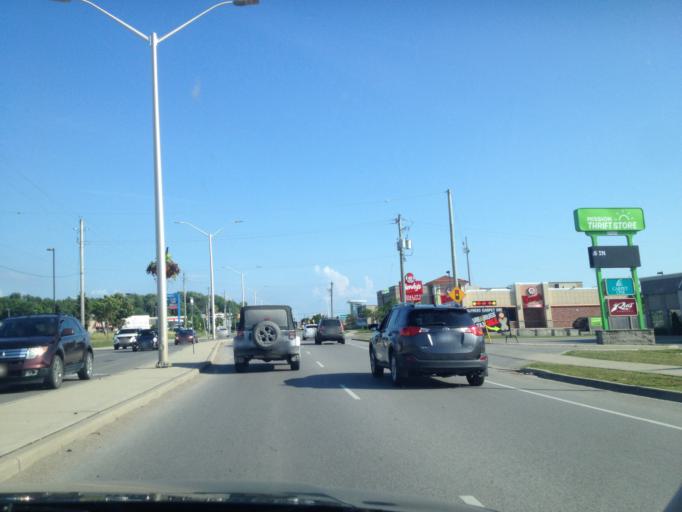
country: CA
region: Ontario
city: London
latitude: 43.0101
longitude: -81.3379
